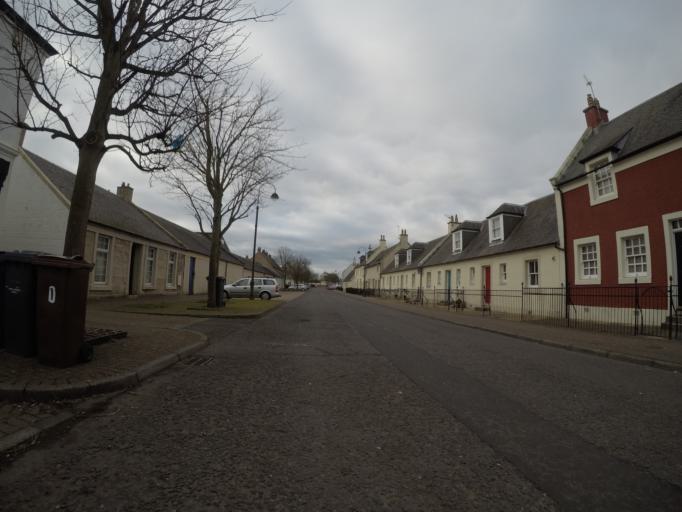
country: GB
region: Scotland
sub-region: North Ayrshire
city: Irvine
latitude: 55.6093
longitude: -4.6785
